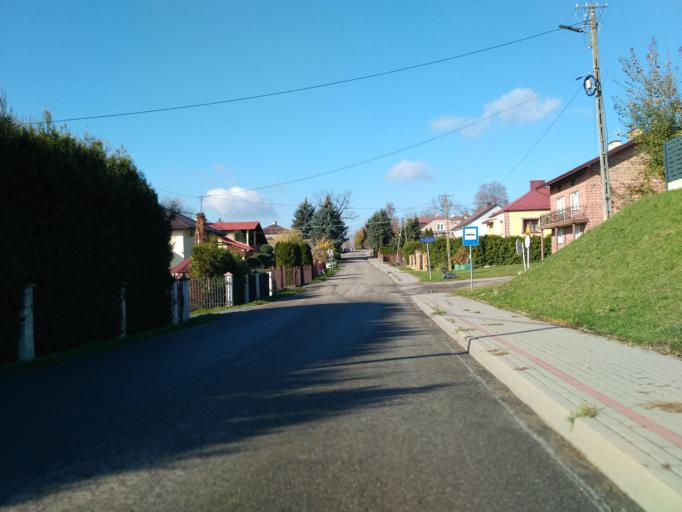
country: PL
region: Subcarpathian Voivodeship
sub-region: Powiat rzeszowski
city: Zglobien
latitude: 50.0269
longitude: 21.8663
